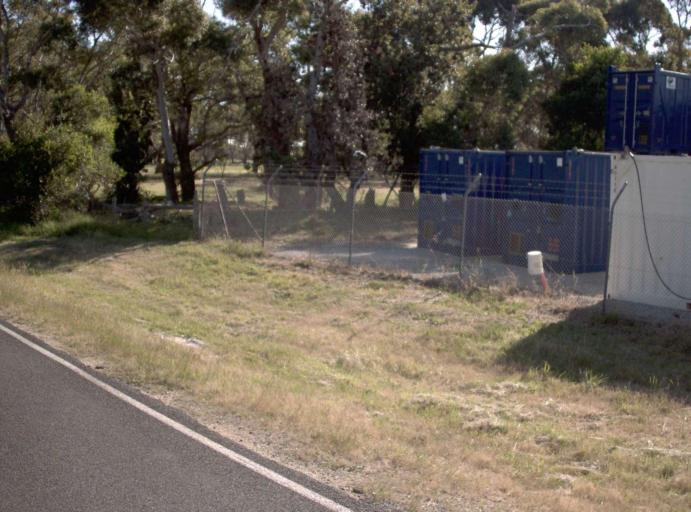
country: AU
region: Victoria
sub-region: Latrobe
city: Morwell
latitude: -38.6970
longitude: 146.3995
